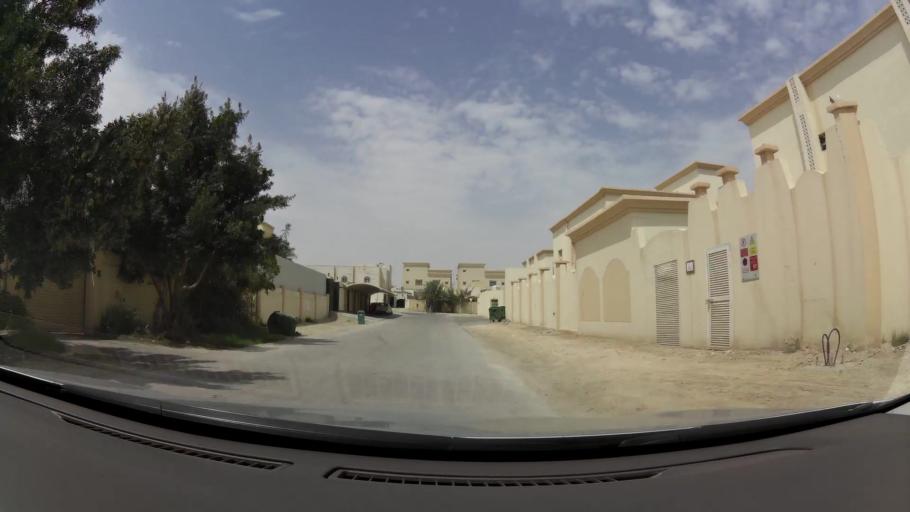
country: QA
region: Baladiyat ar Rayyan
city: Ar Rayyan
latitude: 25.3545
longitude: 51.4698
